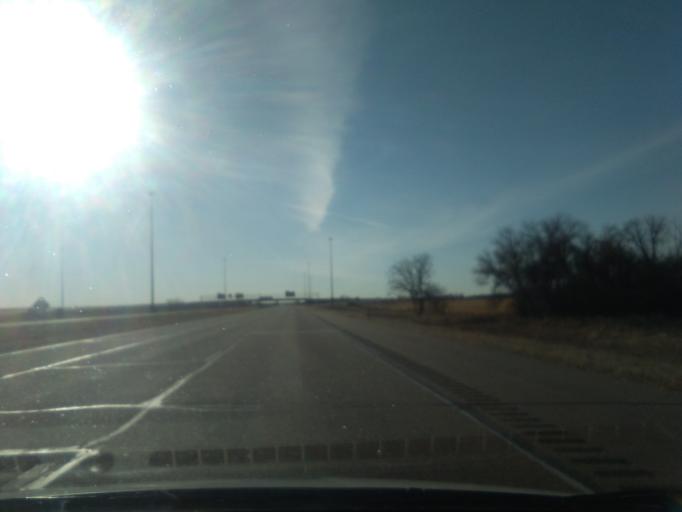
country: US
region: Colorado
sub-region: Sedgwick County
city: Julesburg
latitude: 41.0310
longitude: -102.1477
